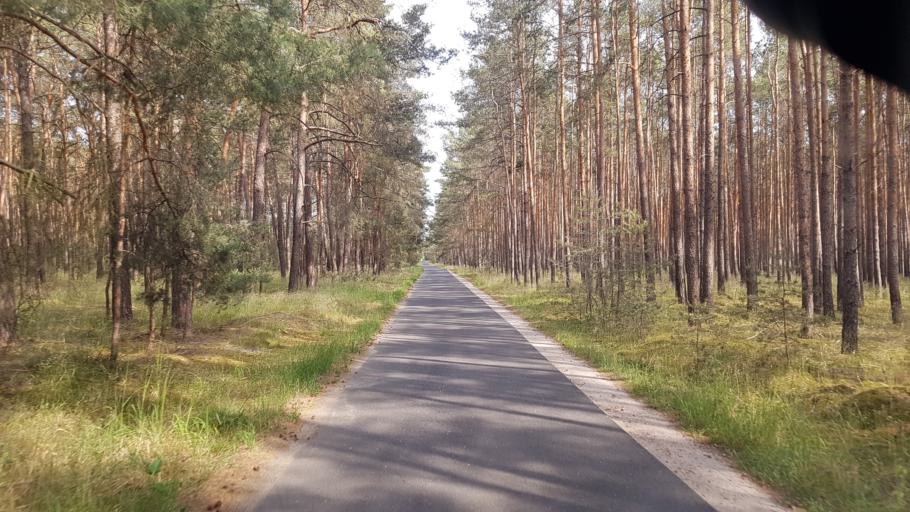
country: DE
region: Brandenburg
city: Herzberg
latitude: 51.7676
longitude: 13.2382
